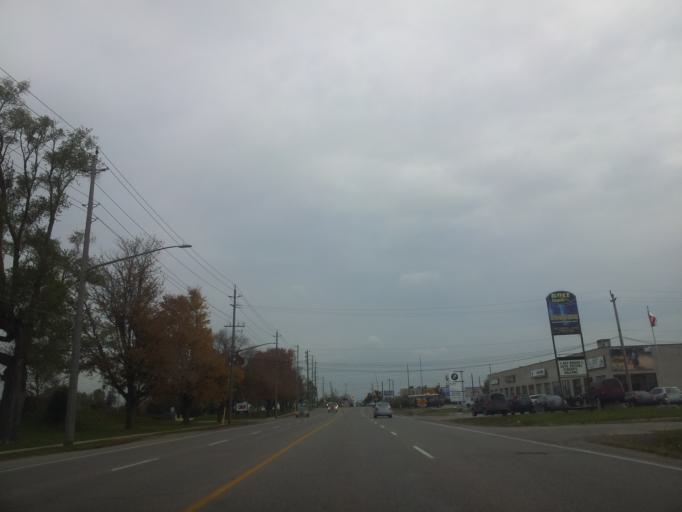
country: CA
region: Ontario
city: London
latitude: 43.0153
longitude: -81.1852
